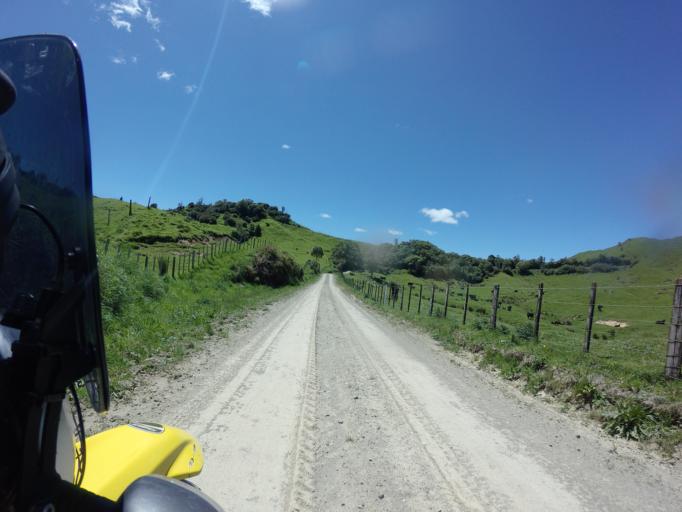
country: NZ
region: Bay of Plenty
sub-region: Opotiki District
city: Opotiki
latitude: -38.4079
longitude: 177.4415
